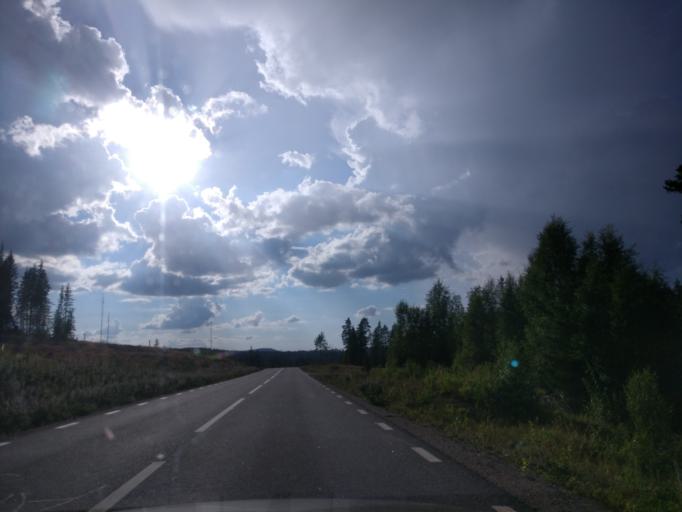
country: SE
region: Dalarna
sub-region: Ludvika Kommun
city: Abborrberget
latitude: 60.1806
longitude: 14.6905
